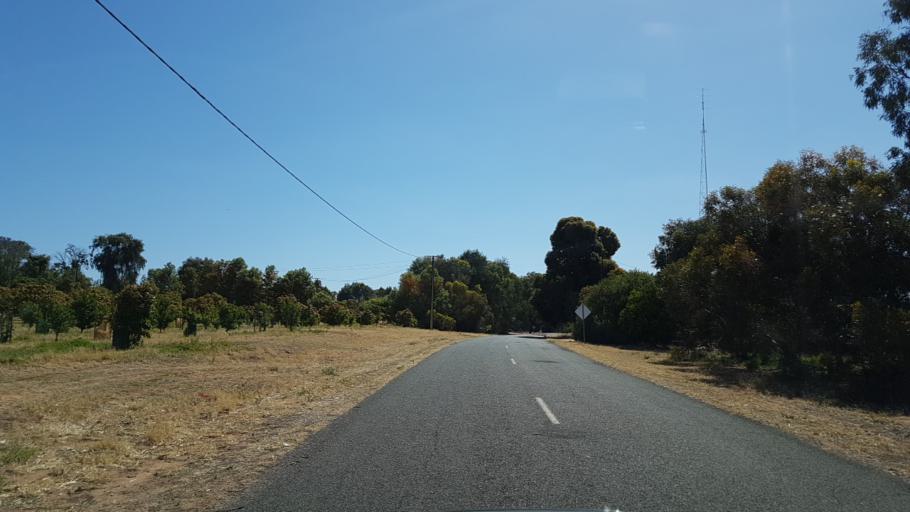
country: AU
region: South Australia
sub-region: Loxton Waikerie
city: Waikerie
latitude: -34.1657
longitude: 140.0288
